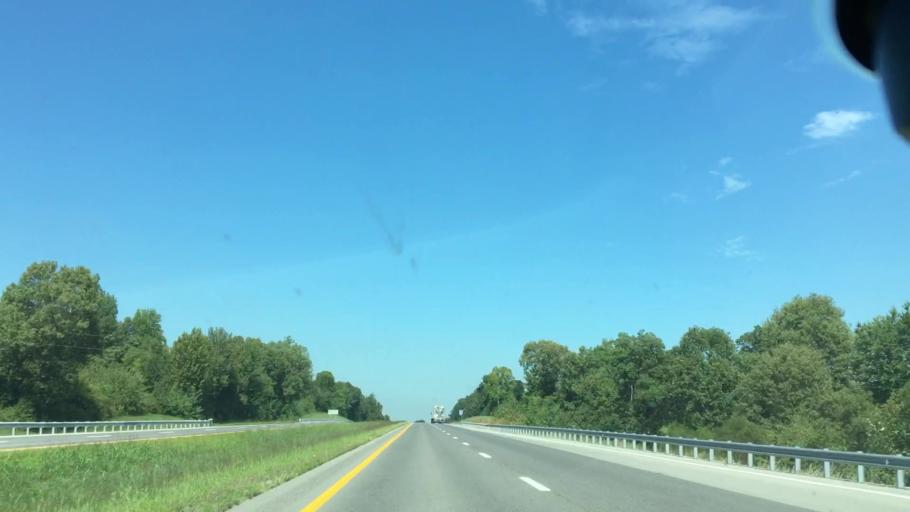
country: US
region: Kentucky
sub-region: Webster County
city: Sebree
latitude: 37.4944
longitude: -87.4753
